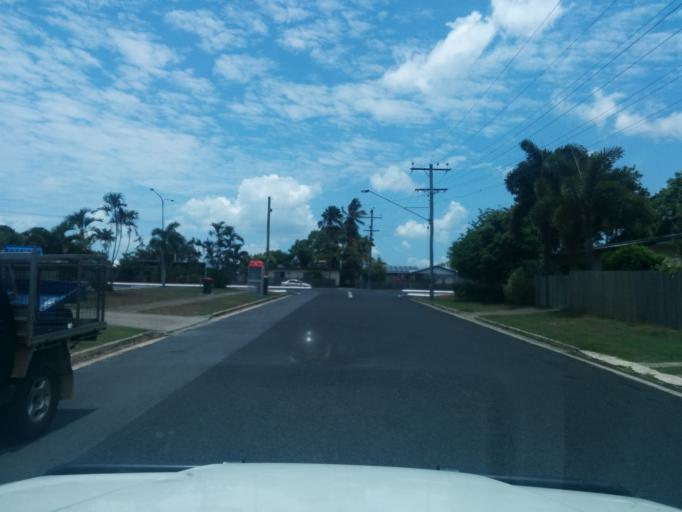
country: AU
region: Queensland
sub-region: Cairns
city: Trinity Beach
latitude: -16.8046
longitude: 145.7010
